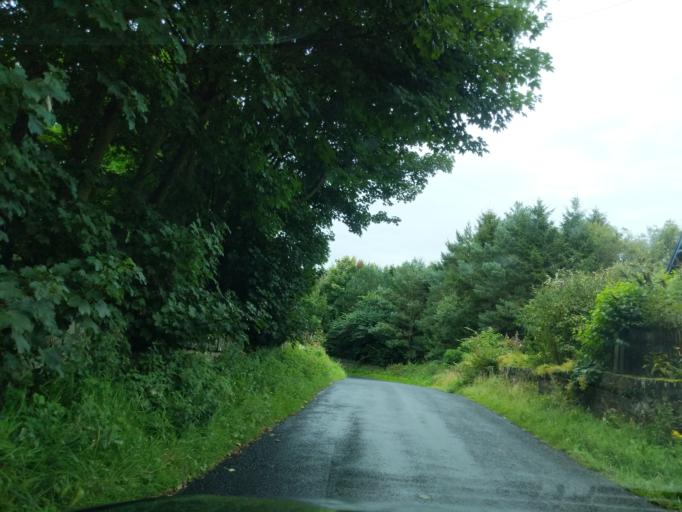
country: GB
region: Scotland
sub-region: Fife
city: Limekilns
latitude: 55.9882
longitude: -3.4652
